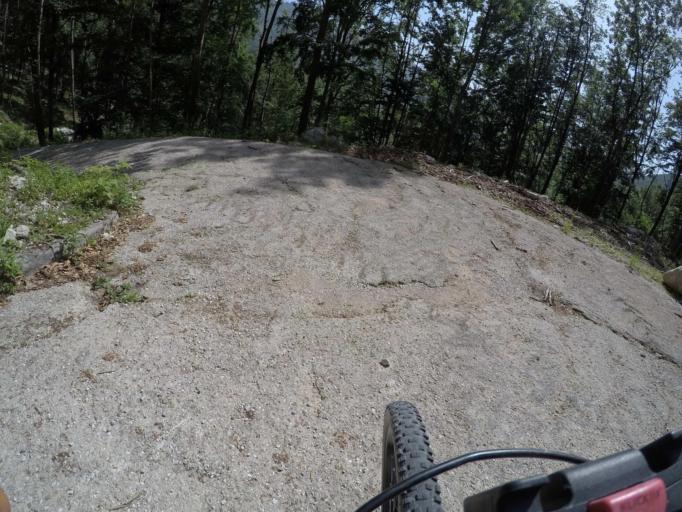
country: IT
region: Friuli Venezia Giulia
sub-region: Provincia di Udine
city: Lusevera
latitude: 46.3124
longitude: 13.2411
